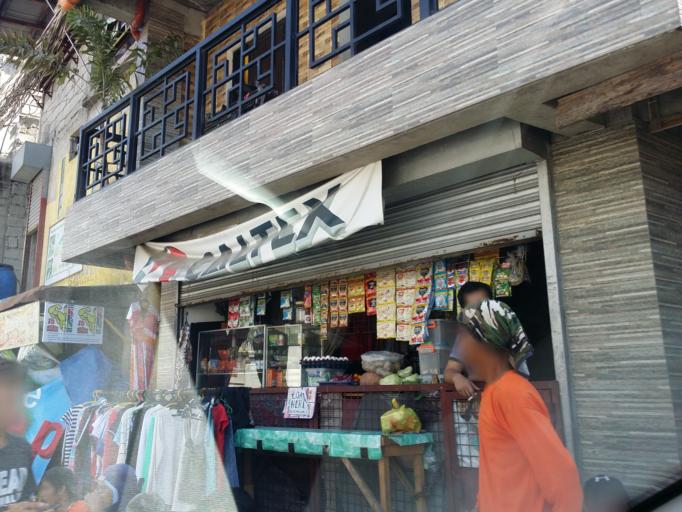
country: PH
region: Metro Manila
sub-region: Mandaluyong
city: Mandaluyong City
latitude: 14.5837
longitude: 121.0352
